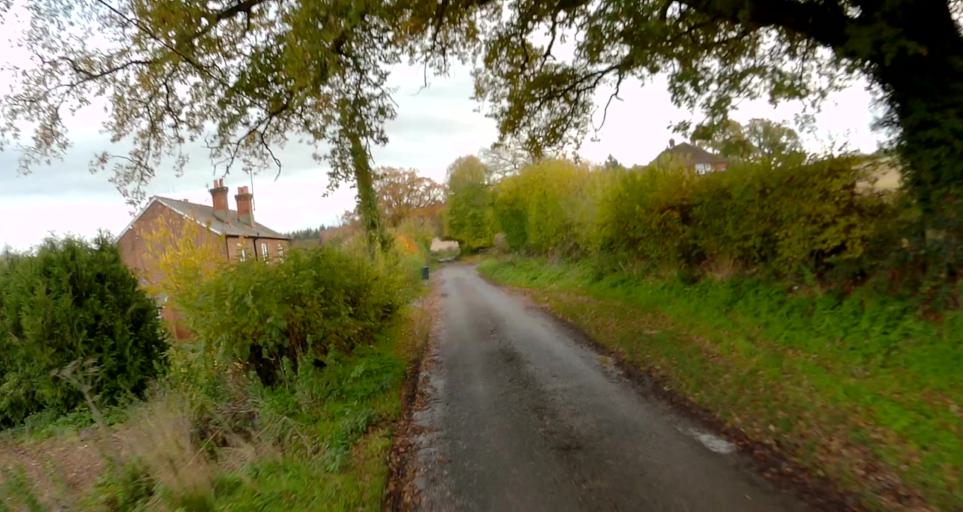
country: GB
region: England
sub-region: Hampshire
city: Long Sutton
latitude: 51.2107
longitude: -0.9565
